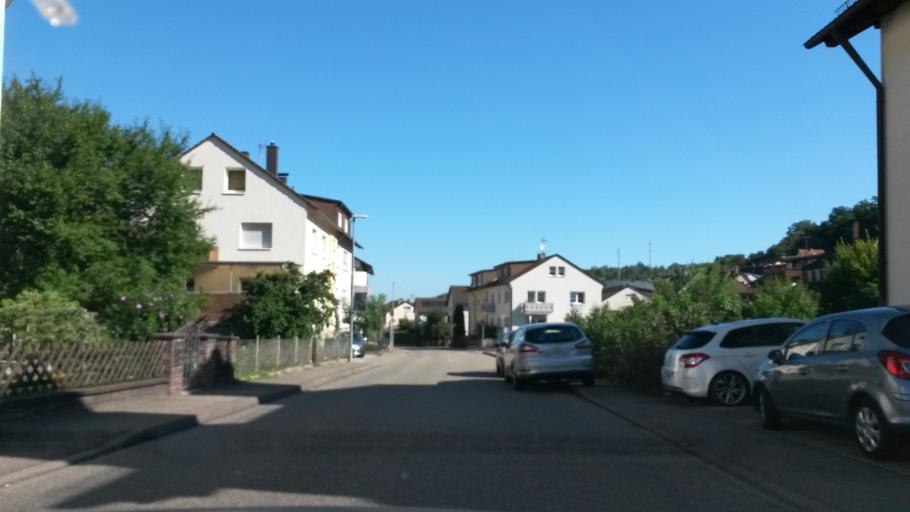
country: DE
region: Baden-Wuerttemberg
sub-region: Karlsruhe Region
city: Ispringen
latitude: 48.9285
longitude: 8.6334
